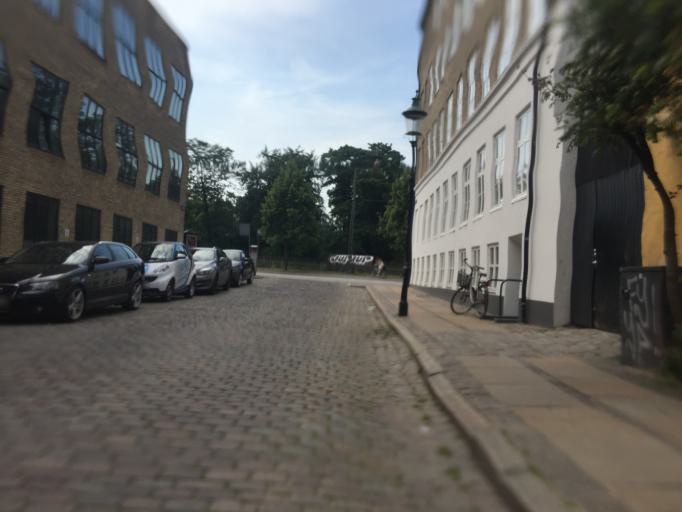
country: DK
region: Capital Region
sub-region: Kobenhavn
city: Christianshavn
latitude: 55.6891
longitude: 12.5827
